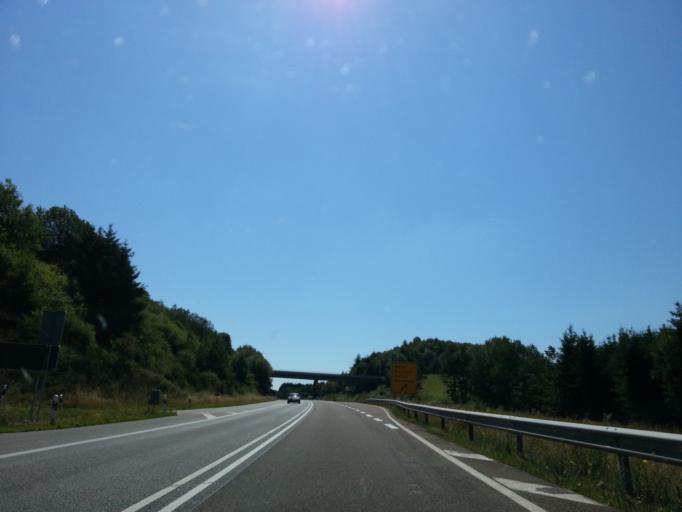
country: DE
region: Rheinland-Pfalz
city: Grosslangenfeld
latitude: 50.2037
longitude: 6.2499
